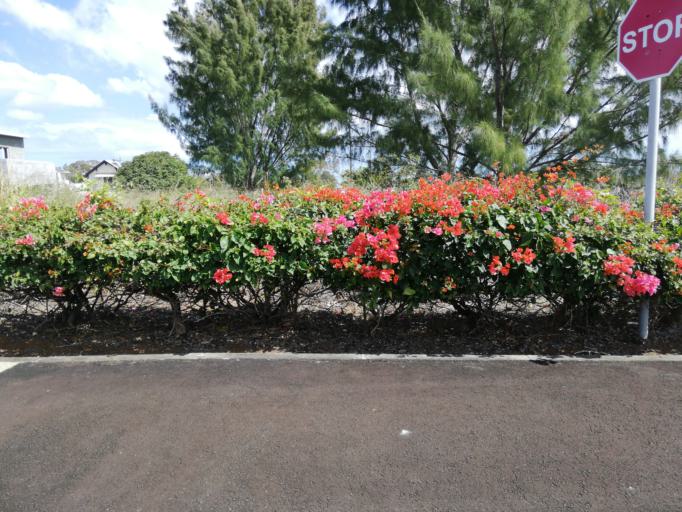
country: MU
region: Moka
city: Moka
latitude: -20.2250
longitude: 57.4812
